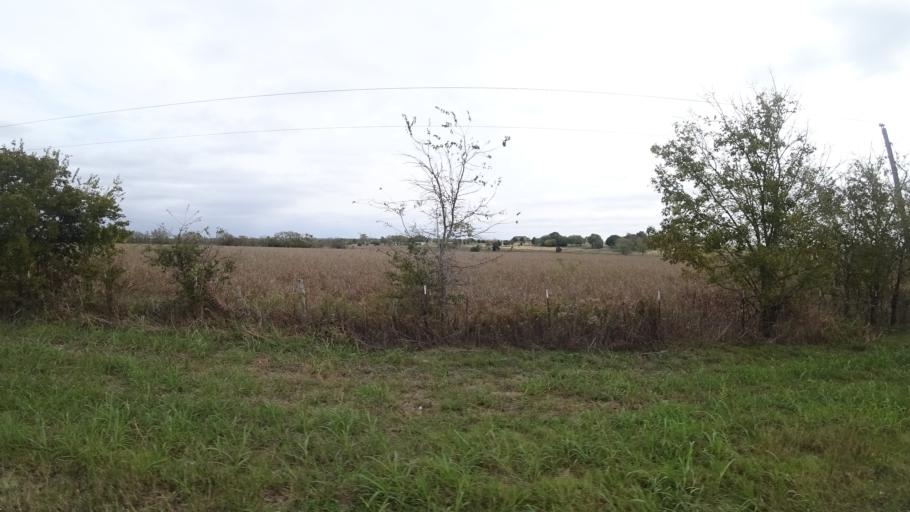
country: US
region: Texas
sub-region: Travis County
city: Manor
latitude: 30.3679
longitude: -97.5681
